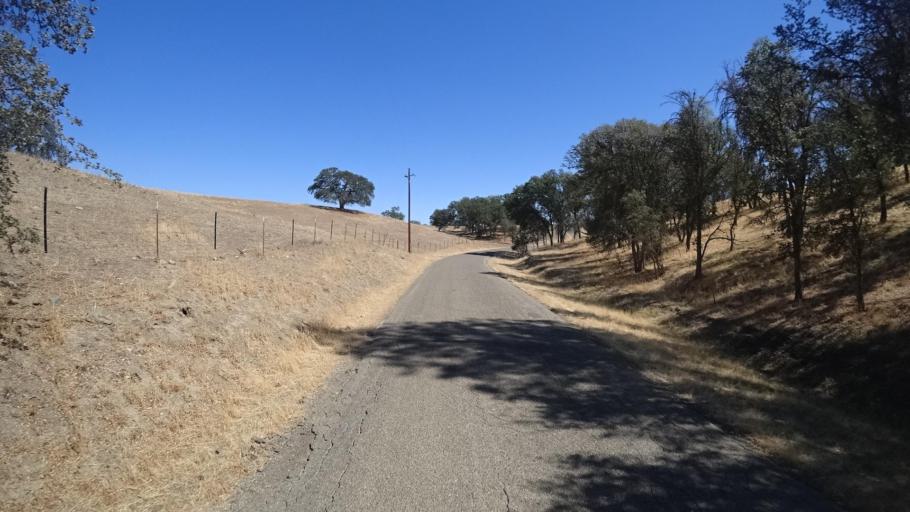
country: US
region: California
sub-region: San Luis Obispo County
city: Shandon
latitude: 35.8788
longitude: -120.4101
